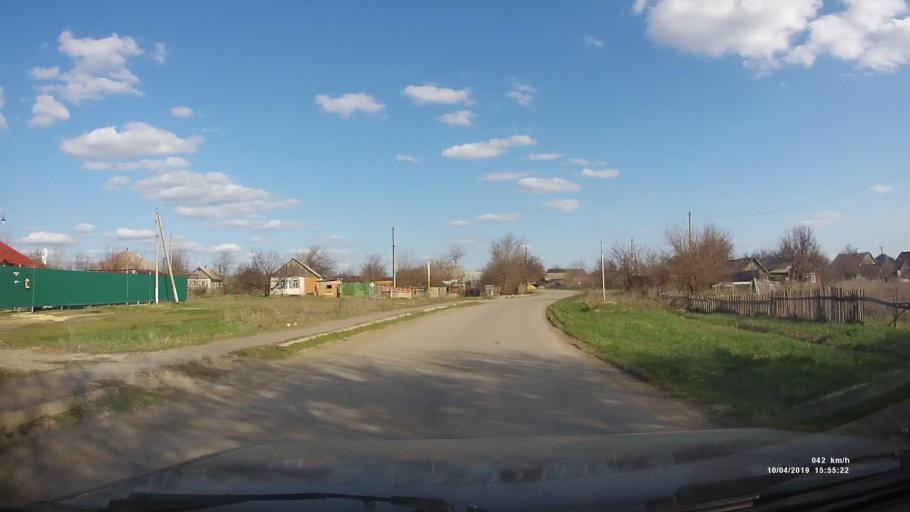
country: RU
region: Rostov
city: Masalovka
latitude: 48.4129
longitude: 40.2645
